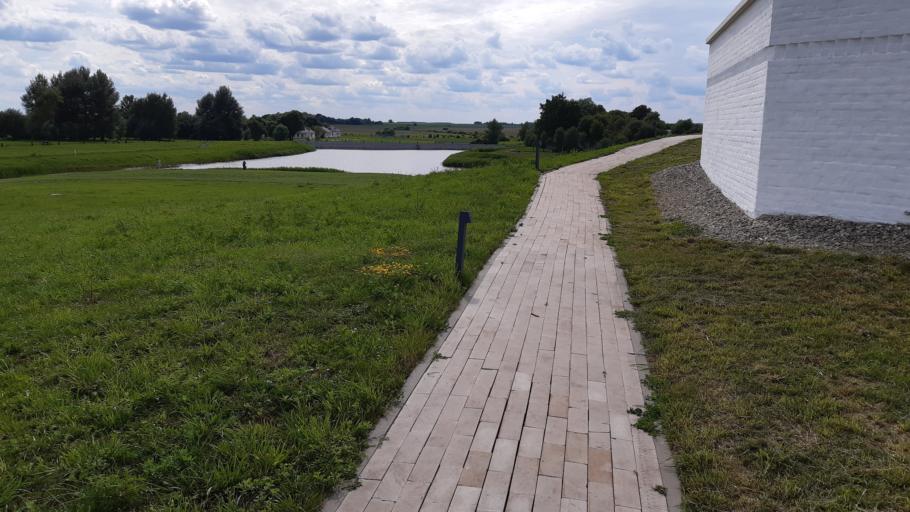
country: RU
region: Tula
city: Kurkino
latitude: 53.6246
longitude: 38.6729
